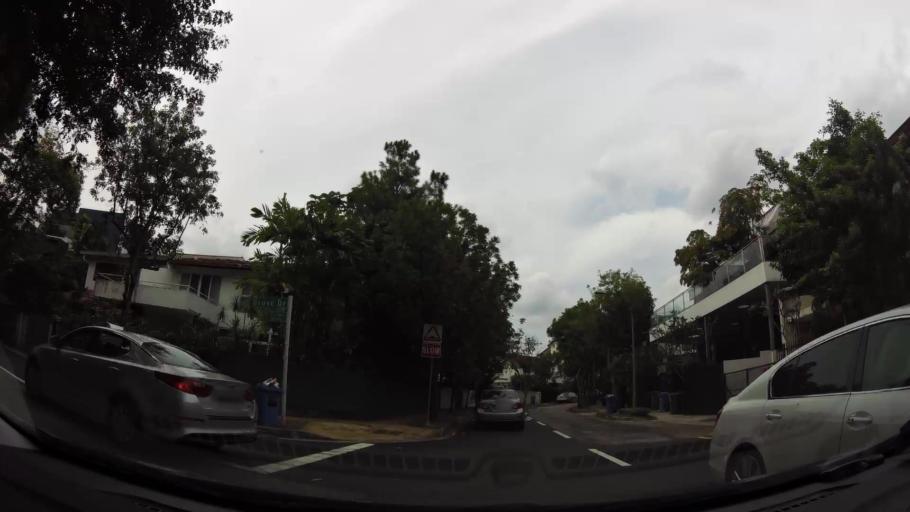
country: SG
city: Singapore
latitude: 1.3128
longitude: 103.7830
